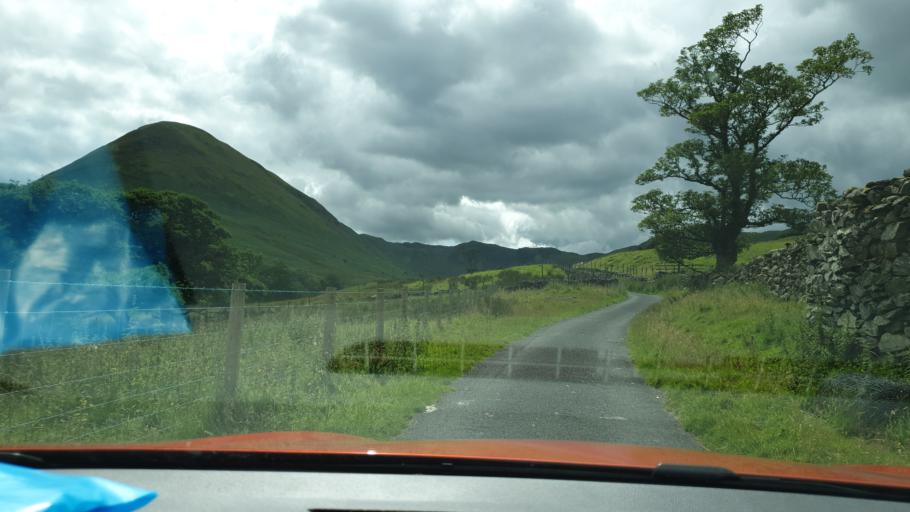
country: GB
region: England
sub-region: Cumbria
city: Ambleside
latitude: 54.5428
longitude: -2.8747
